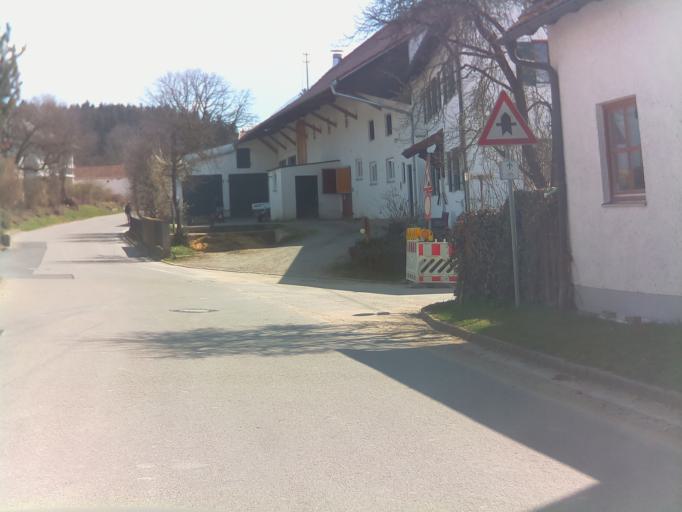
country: DE
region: Bavaria
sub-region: Swabia
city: Aindling
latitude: 48.5223
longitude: 10.9771
